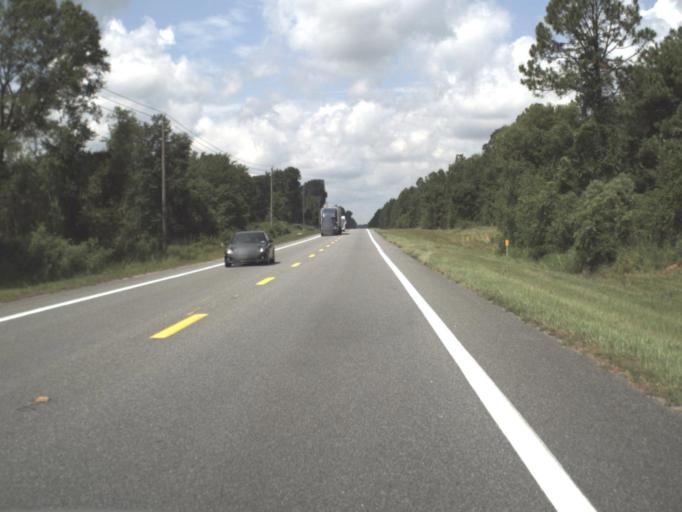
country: US
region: Florida
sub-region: Union County
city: Lake Butler
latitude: 30.0562
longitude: -82.2523
